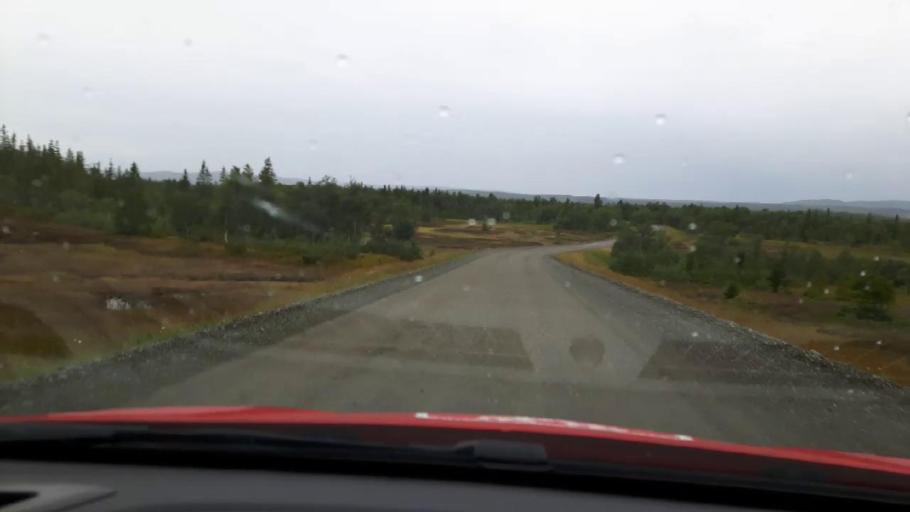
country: NO
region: Nord-Trondelag
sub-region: Meraker
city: Meraker
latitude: 63.5854
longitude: 12.2678
